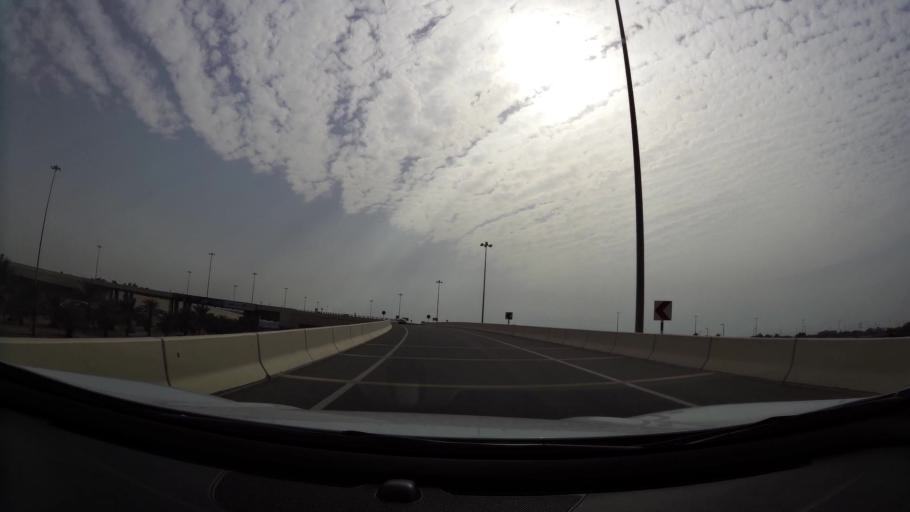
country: AE
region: Abu Dhabi
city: Abu Dhabi
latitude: 24.5130
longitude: 54.6642
